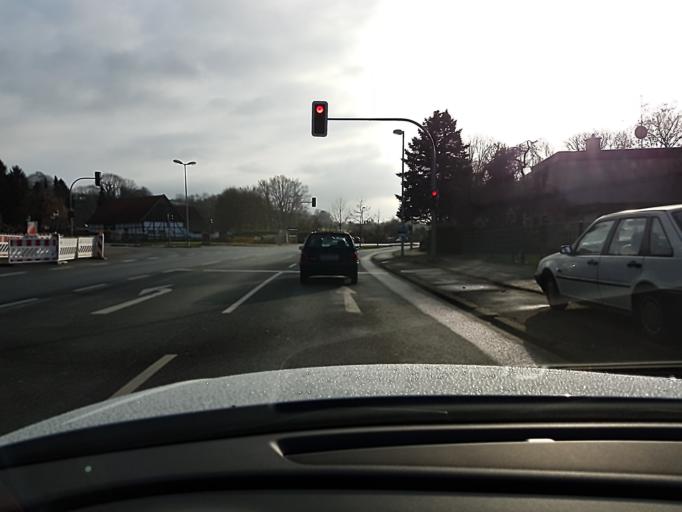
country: DE
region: North Rhine-Westphalia
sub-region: Regierungsbezirk Dusseldorf
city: Muelheim (Ruhr)
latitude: 51.4043
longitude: 6.8985
